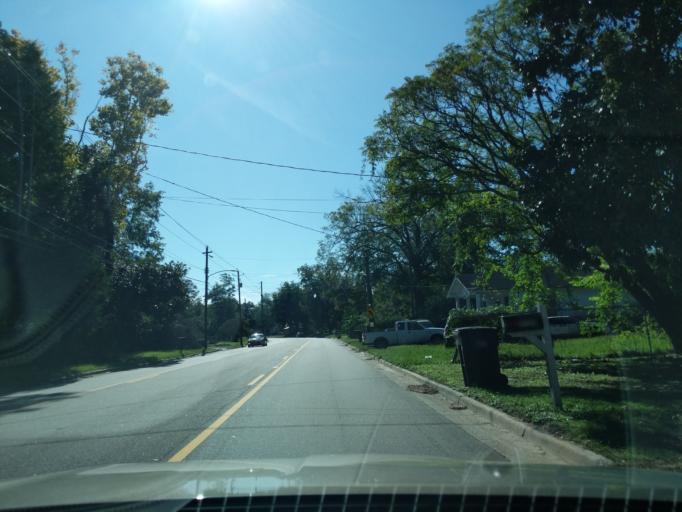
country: US
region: Georgia
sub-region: Richmond County
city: Augusta
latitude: 33.4449
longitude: -82.0053
